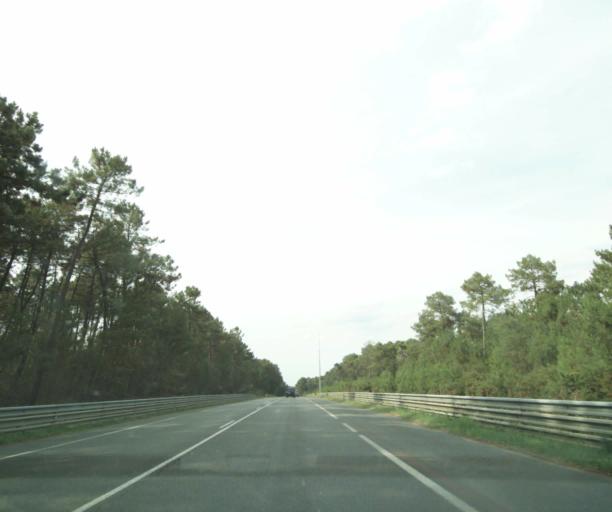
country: FR
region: Pays de la Loire
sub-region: Departement de la Sarthe
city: Mulsanne
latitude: 47.9170
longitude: 0.2438
